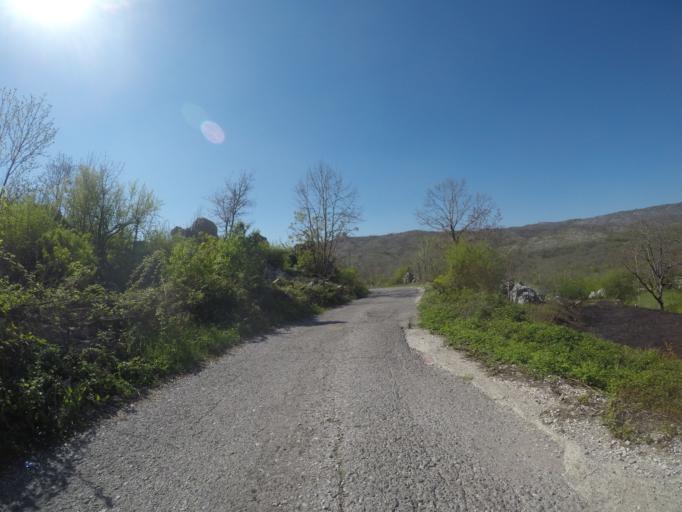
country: ME
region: Danilovgrad
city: Danilovgrad
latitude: 42.5231
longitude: 19.0496
